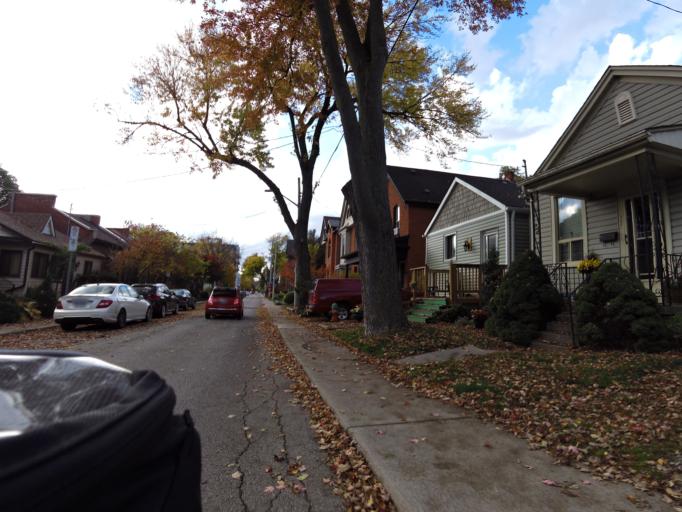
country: CA
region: Ontario
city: Hamilton
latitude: 43.2575
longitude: -79.8820
